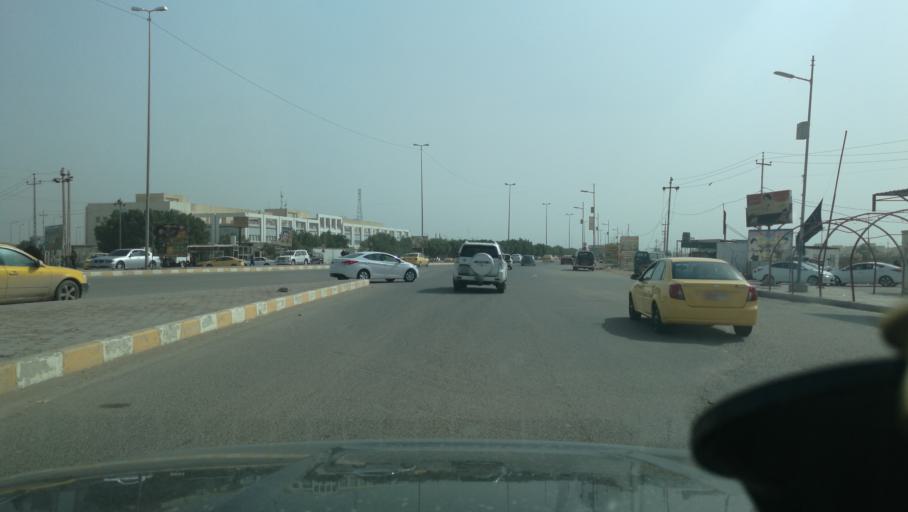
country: IQ
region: Dhi Qar
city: An Nasiriyah
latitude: 31.0826
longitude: 46.2463
